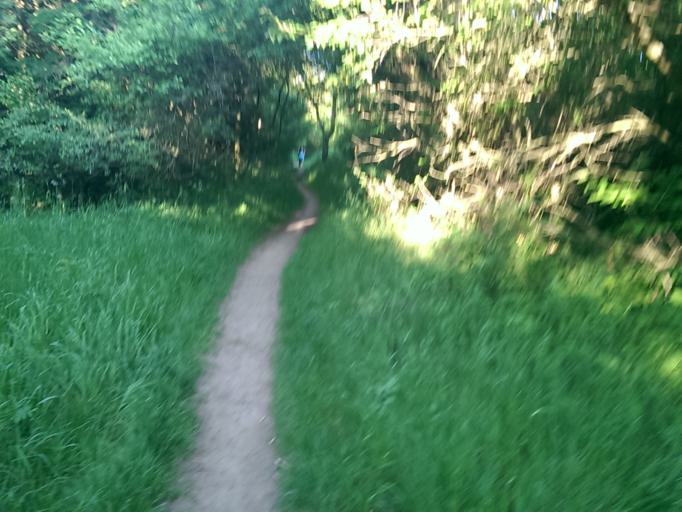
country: CZ
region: Praha
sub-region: Praha 9
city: Vysocany
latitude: 50.0488
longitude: 14.5116
